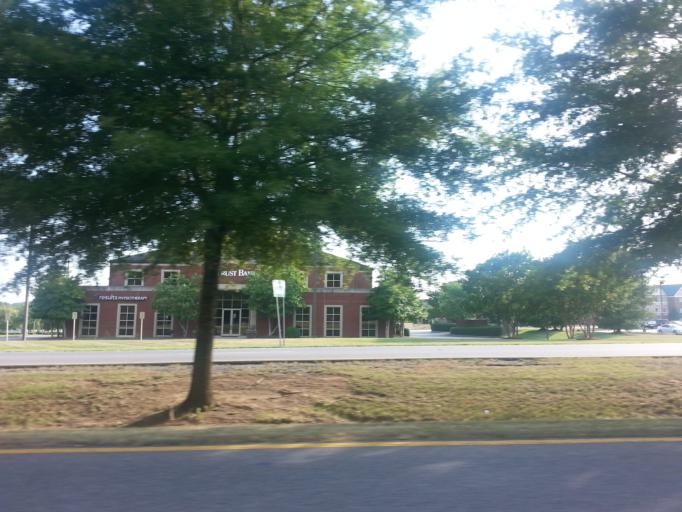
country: US
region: Tennessee
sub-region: Blount County
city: Alcoa
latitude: 35.7849
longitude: -83.9871
